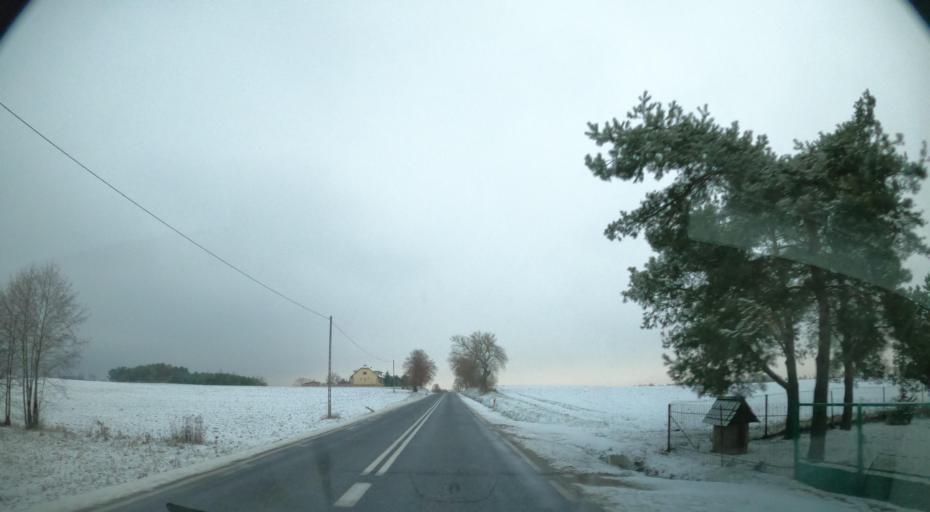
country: PL
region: Masovian Voivodeship
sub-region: Powiat plocki
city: Nowy Duninow
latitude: 52.6297
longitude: 19.4218
